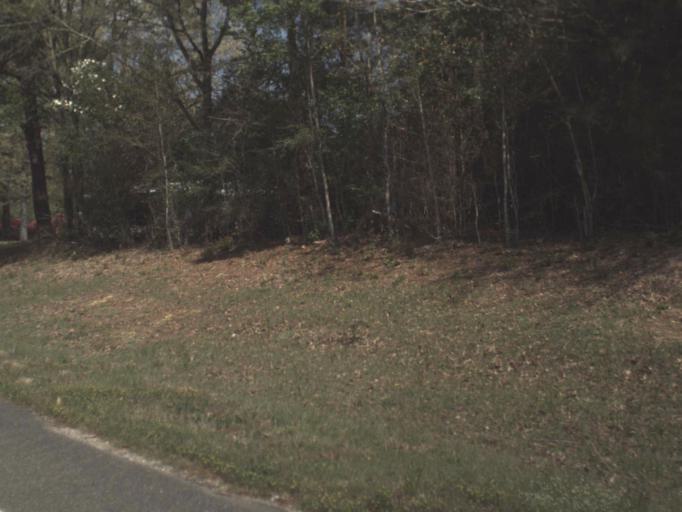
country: US
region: Florida
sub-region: Santa Rosa County
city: Point Baker
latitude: 30.8652
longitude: -86.9113
